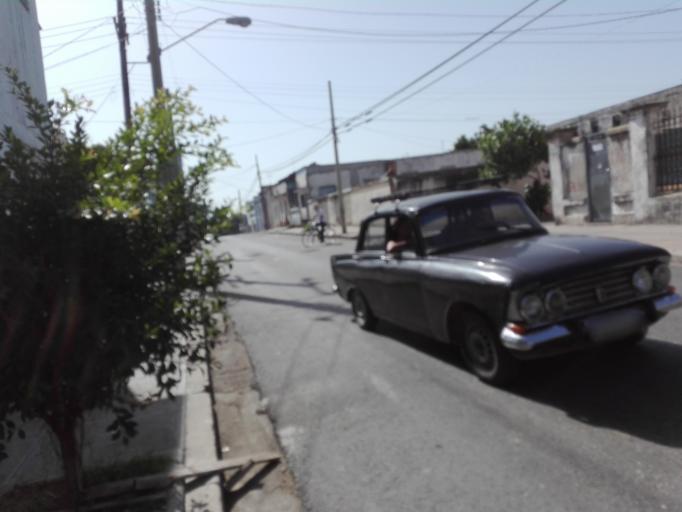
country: CU
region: Cienfuegos
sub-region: Municipio de Cienfuegos
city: Cienfuegos
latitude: 22.1471
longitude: -80.4435
